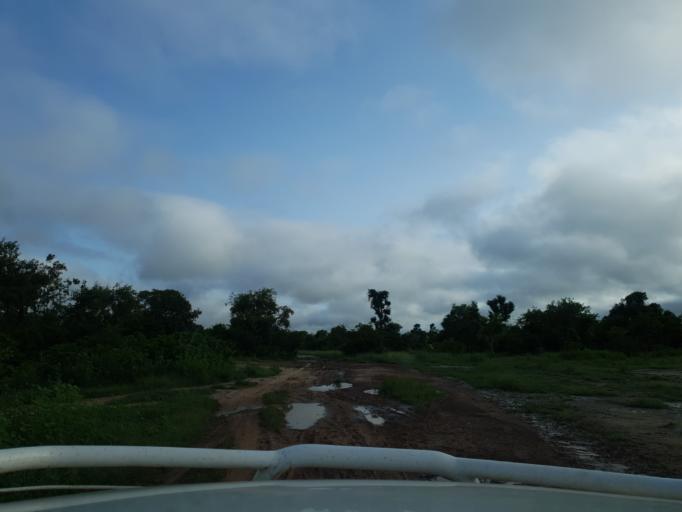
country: ML
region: Segou
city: Baroueli
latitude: 13.3928
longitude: -7.0057
